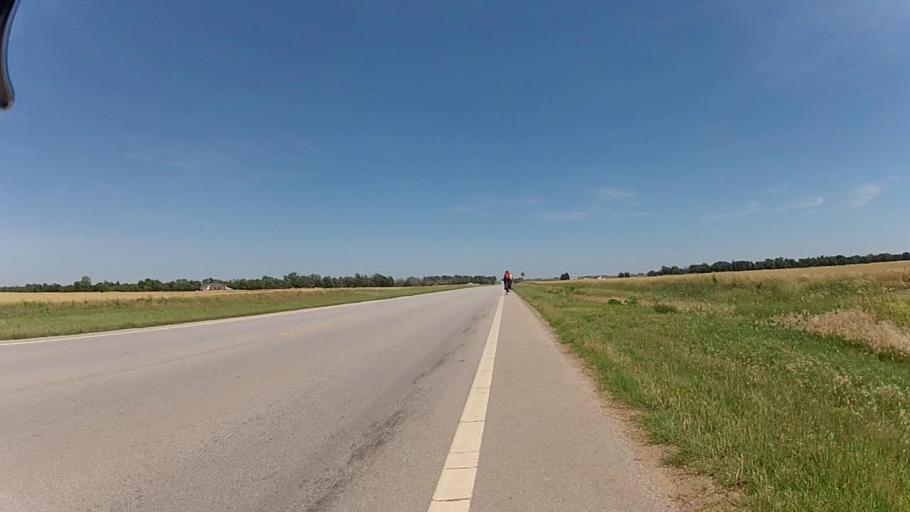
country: US
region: Kansas
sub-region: Harper County
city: Harper
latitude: 37.2386
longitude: -98.1277
